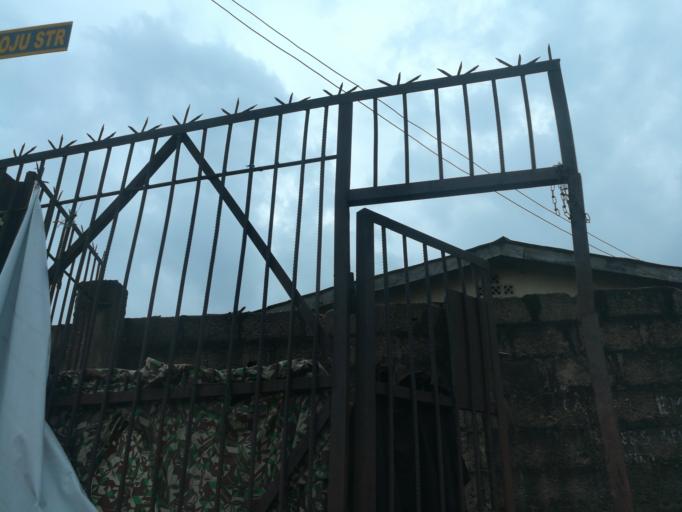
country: NG
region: Lagos
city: Oshodi
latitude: 6.5735
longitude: 3.3433
